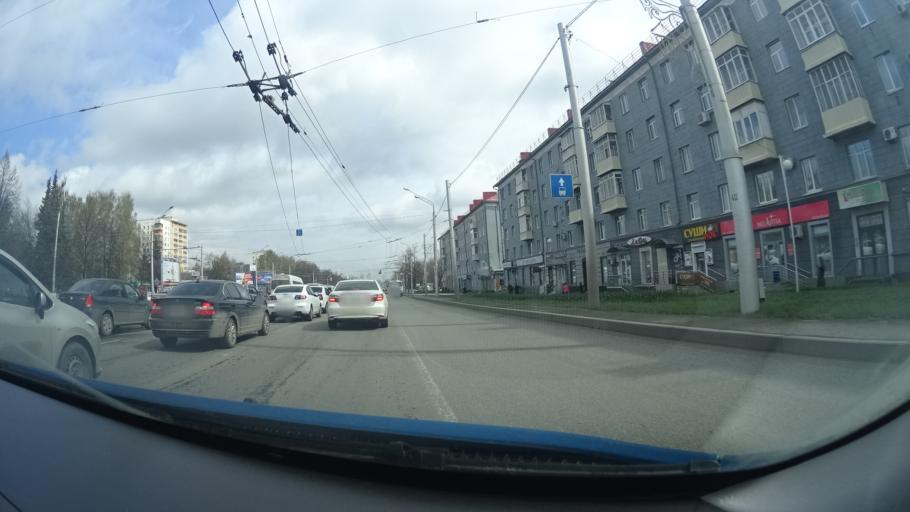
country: RU
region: Bashkortostan
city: Ufa
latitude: 54.7452
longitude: 55.9886
